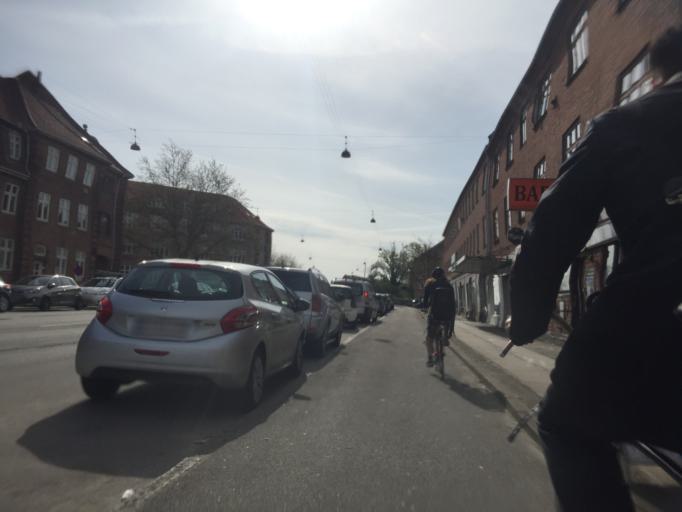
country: DK
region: Capital Region
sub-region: Kobenhavn
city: Vanlose
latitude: 55.6697
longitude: 12.4917
